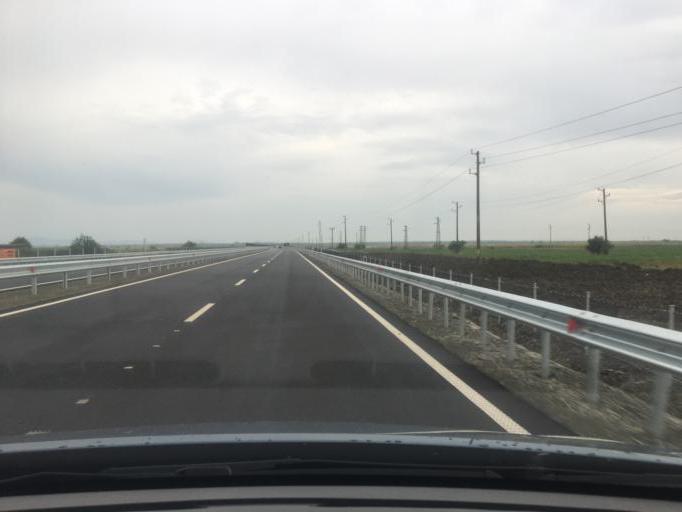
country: BG
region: Burgas
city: Aheloy
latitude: 42.6275
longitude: 27.6316
